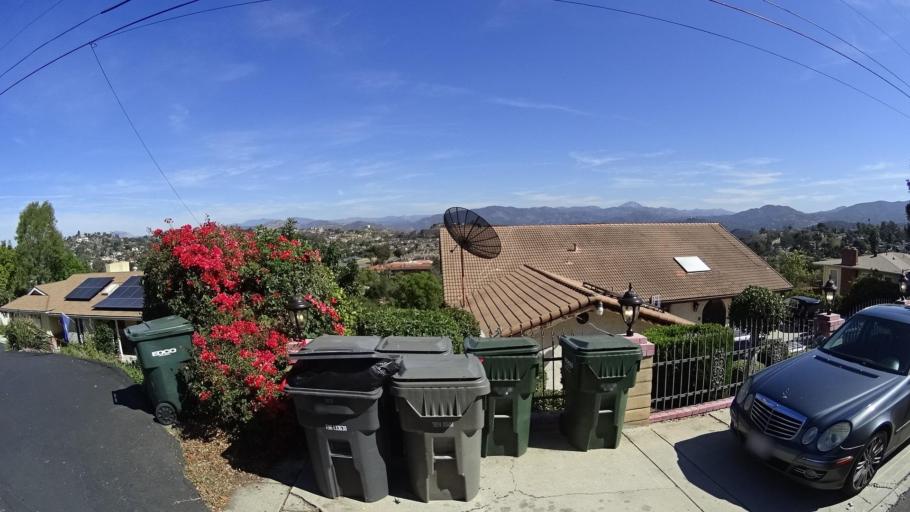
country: US
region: California
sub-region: San Diego County
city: Casa de Oro-Mount Helix
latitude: 32.7475
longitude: -116.9668
